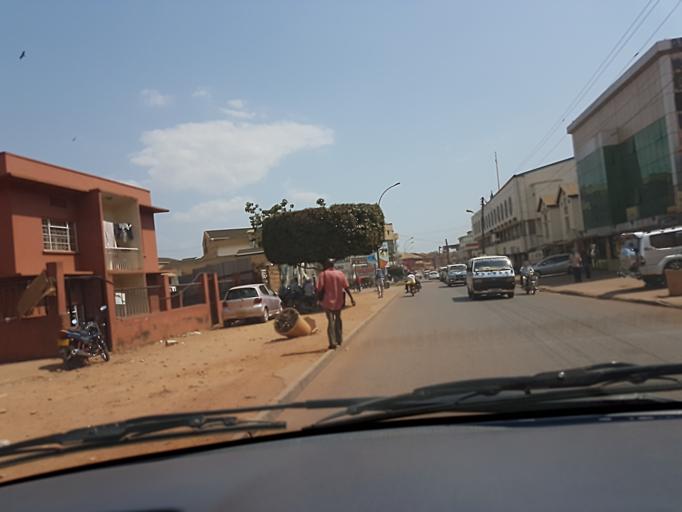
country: UG
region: Central Region
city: Kampala Central Division
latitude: 0.3176
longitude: 32.5707
